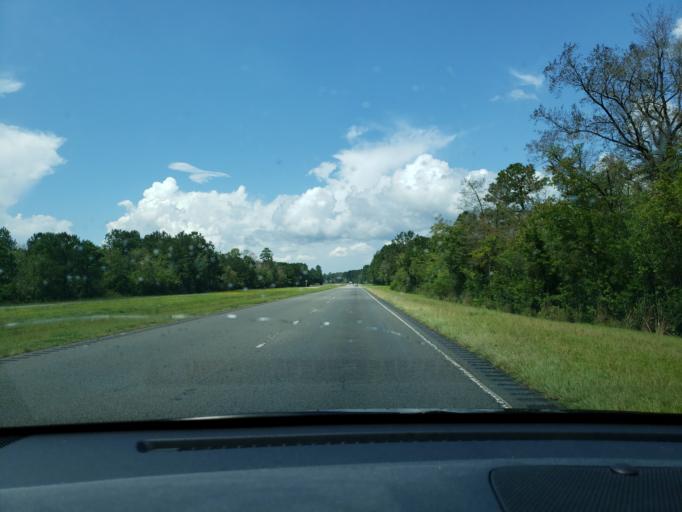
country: US
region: North Carolina
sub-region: Bladen County
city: Elizabethtown
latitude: 34.6396
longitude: -78.6704
